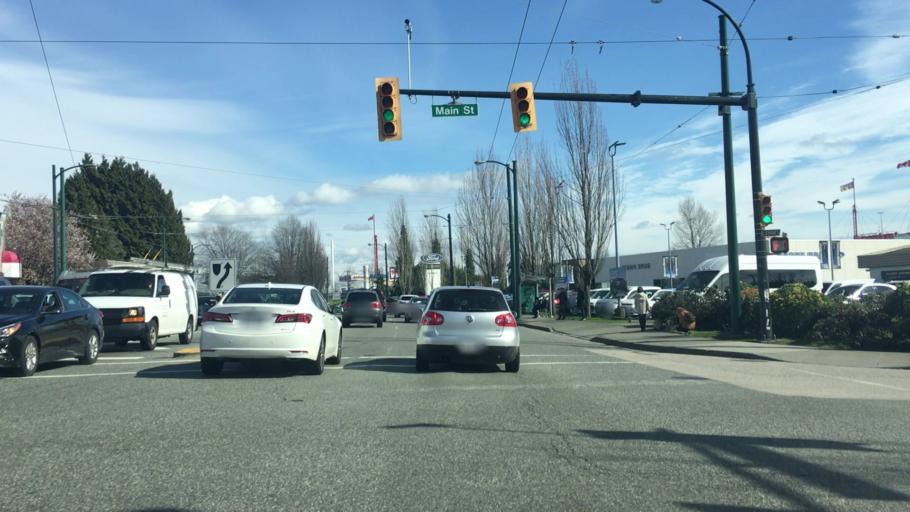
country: CA
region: British Columbia
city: Vancouver
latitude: 49.2110
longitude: -123.1022
